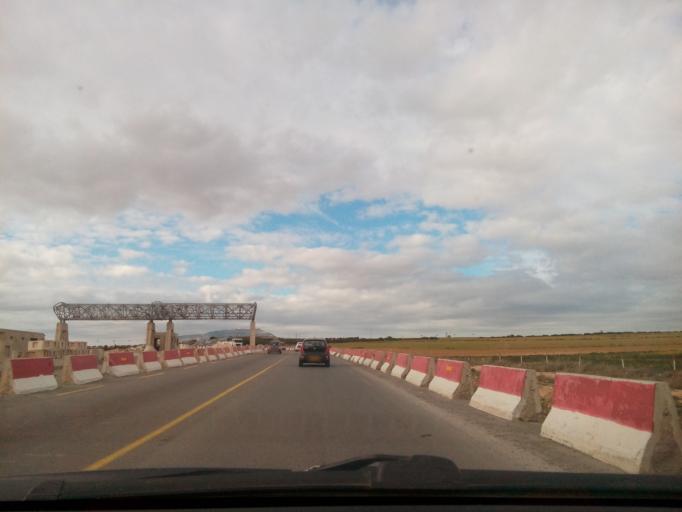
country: DZ
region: Sidi Bel Abbes
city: Sidi Bel Abbes
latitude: 35.2161
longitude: -0.6690
